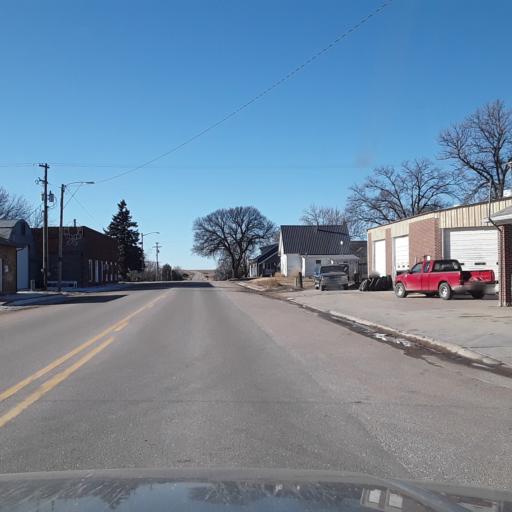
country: US
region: Nebraska
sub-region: Dawson County
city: Gothenburg
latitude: 40.7058
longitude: -100.2146
